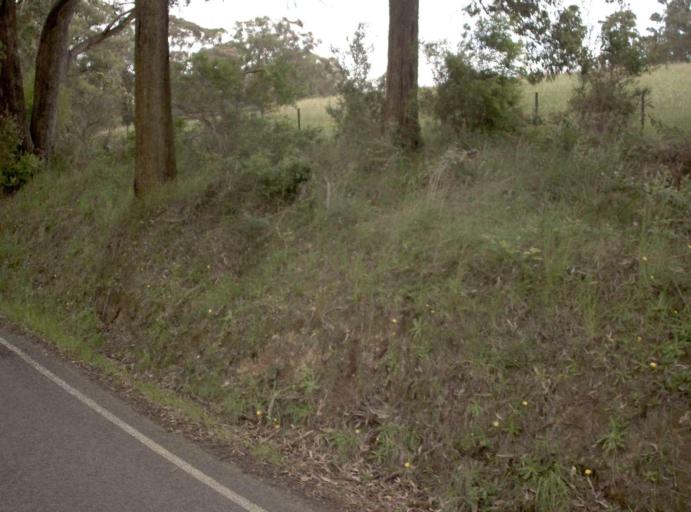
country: AU
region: Victoria
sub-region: Latrobe
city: Moe
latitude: -37.9439
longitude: 146.1171
